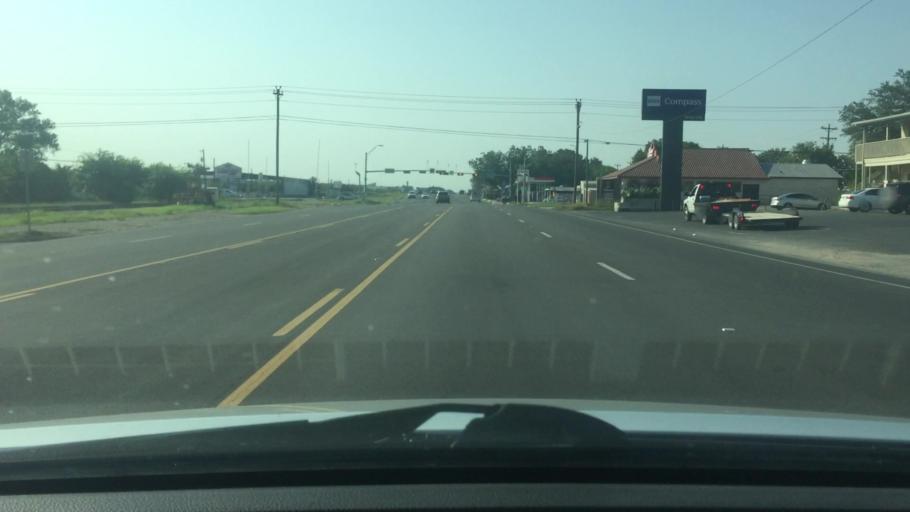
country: US
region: Texas
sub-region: Williamson County
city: Leander
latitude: 30.5802
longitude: -97.8536
